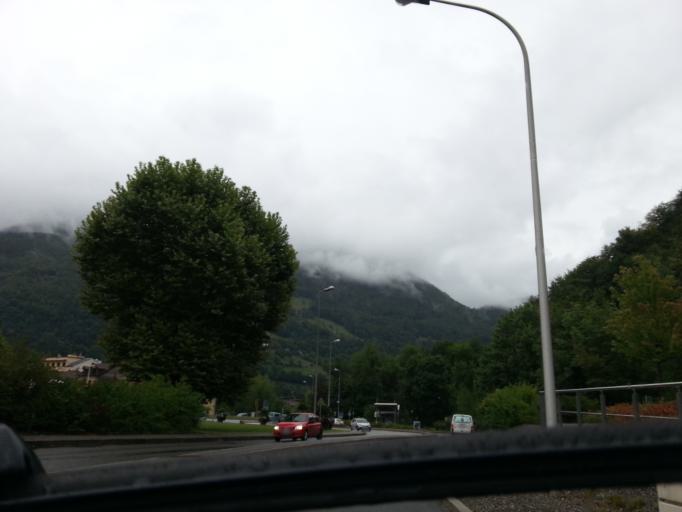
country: FR
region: Rhone-Alpes
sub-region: Departement de la Savoie
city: Ugine
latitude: 45.7460
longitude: 6.4190
